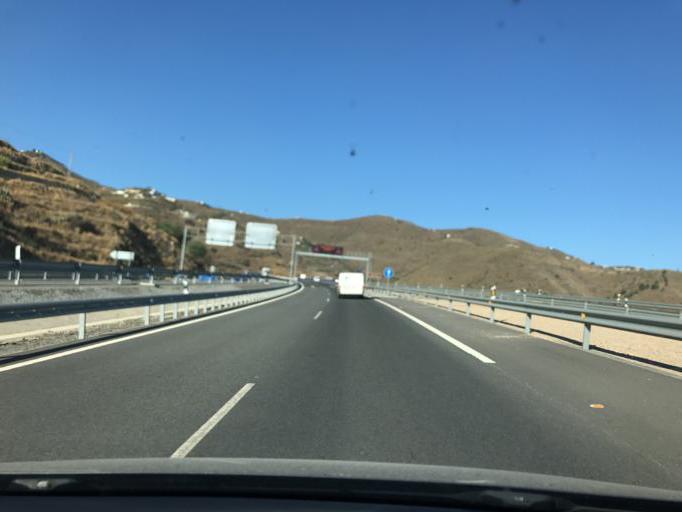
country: ES
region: Andalusia
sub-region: Provincia de Granada
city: Jete
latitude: 36.7584
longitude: -3.6575
